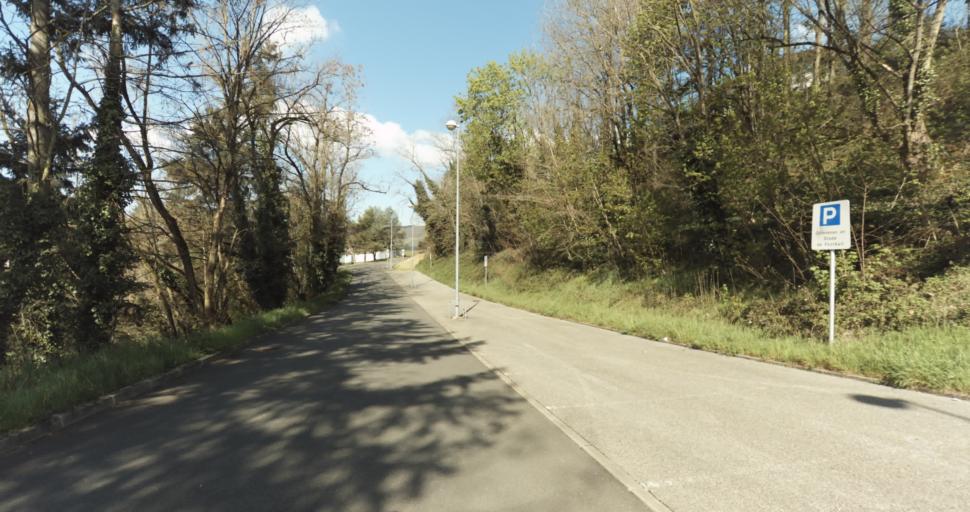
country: FR
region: Rhone-Alpes
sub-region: Departement du Rhone
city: Tarare
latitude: 45.8935
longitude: 4.4456
